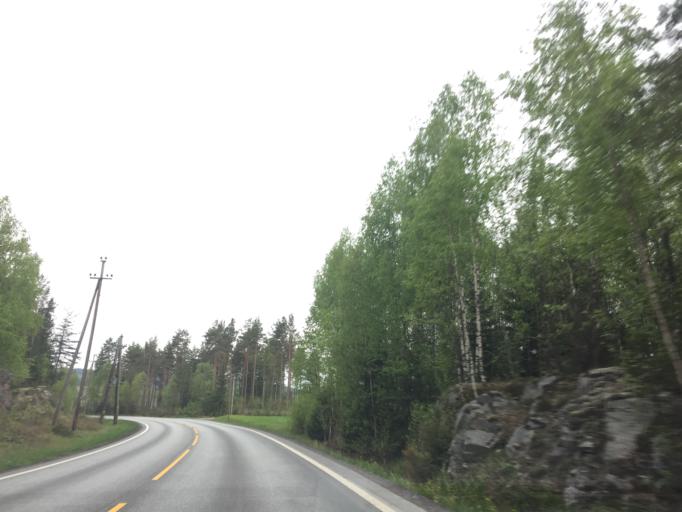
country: NO
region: Akershus
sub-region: Nes
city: Arnes
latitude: 60.1749
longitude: 11.5351
